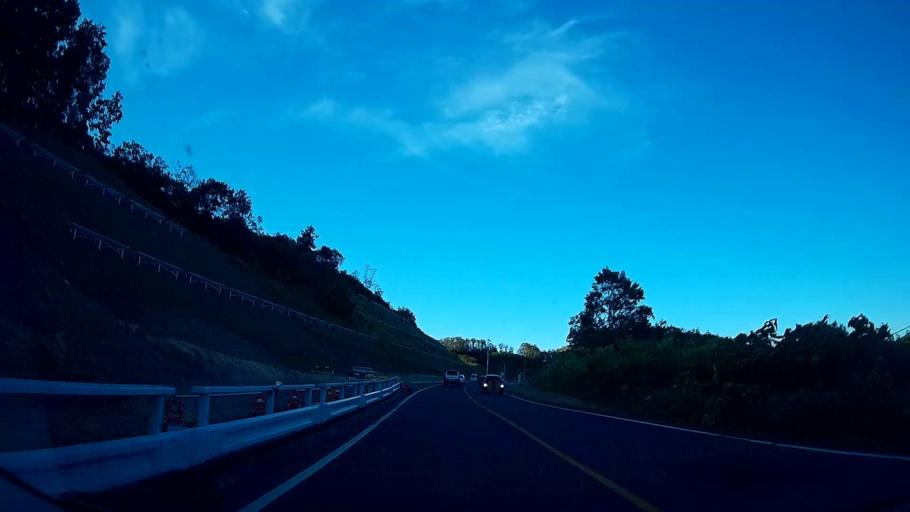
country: JP
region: Hokkaido
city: Yoichi
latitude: 43.2014
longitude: 140.8688
